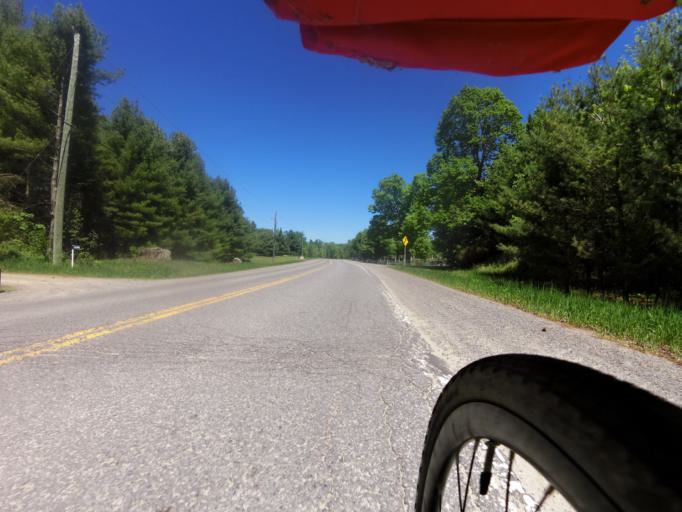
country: CA
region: Ontario
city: Carleton Place
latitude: 45.1864
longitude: -76.3390
